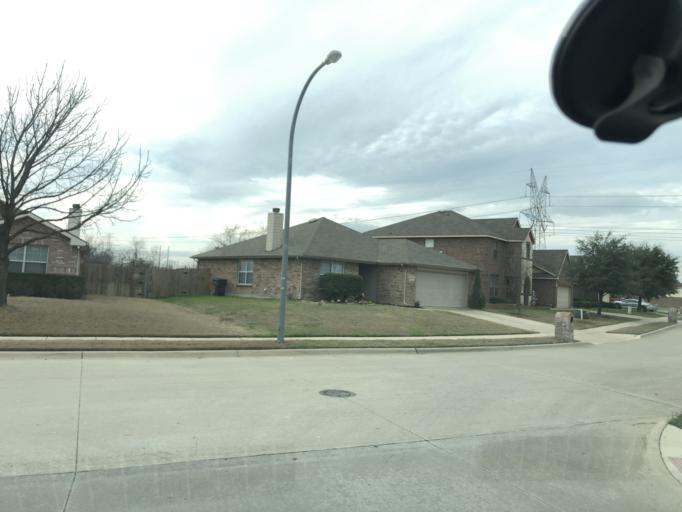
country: US
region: Texas
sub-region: Tarrant County
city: Saginaw
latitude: 32.9061
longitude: -97.3707
